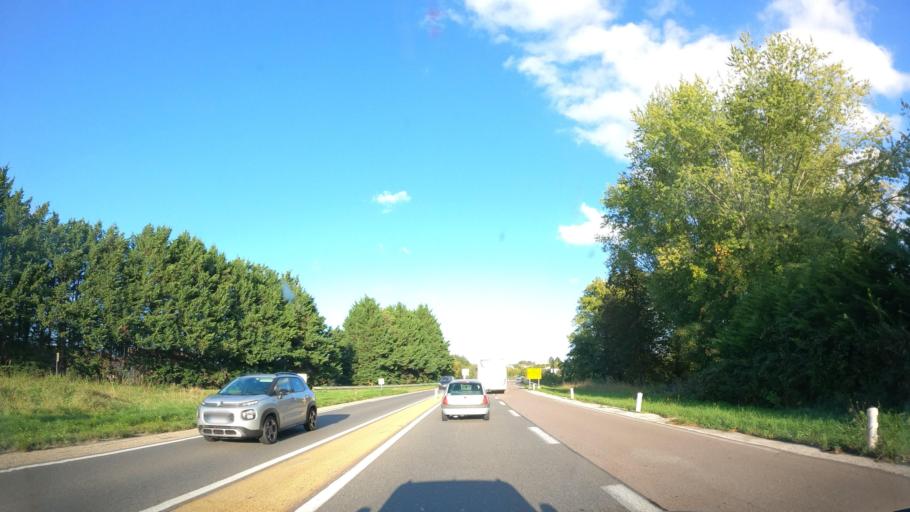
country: FR
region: Bourgogne
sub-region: Departement de Saone-et-Loire
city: Blanzy
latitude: 46.7012
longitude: 4.3920
